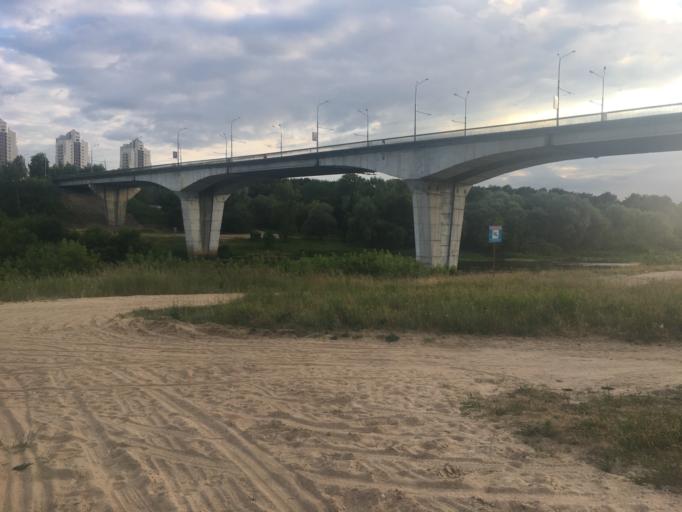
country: BY
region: Grodnenskaya
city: Hrodna
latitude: 53.6798
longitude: 23.8079
